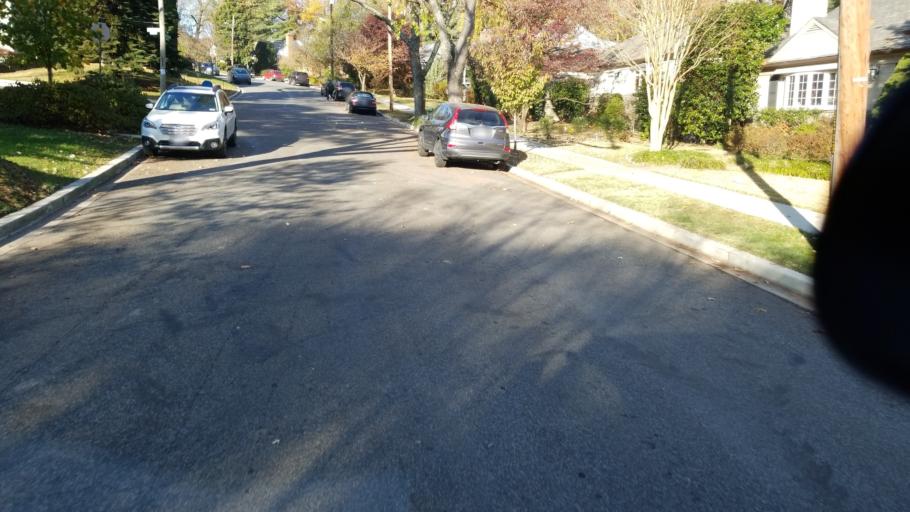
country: US
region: Maryland
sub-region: Montgomery County
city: Chevy Chase
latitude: 38.9574
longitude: -77.0653
